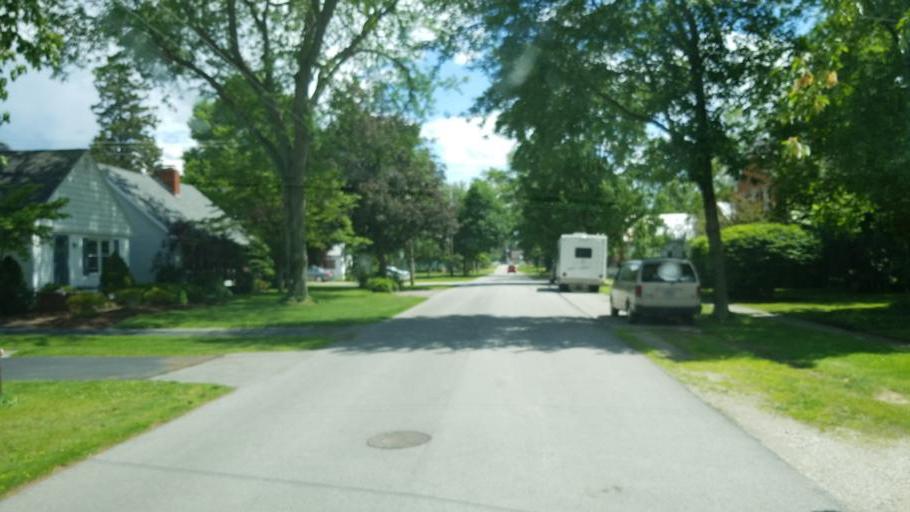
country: US
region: Ohio
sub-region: Erie County
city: Milan
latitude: 41.2946
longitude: -82.6050
